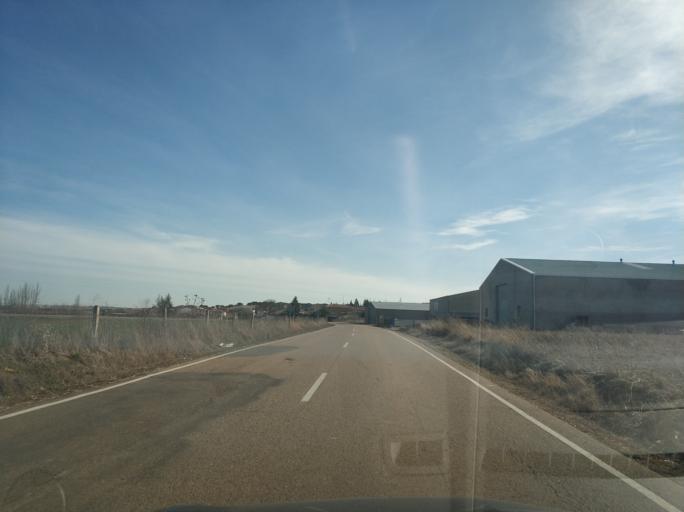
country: ES
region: Castille and Leon
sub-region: Provincia de Salamanca
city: Florida de Liebana
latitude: 41.0296
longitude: -5.7641
